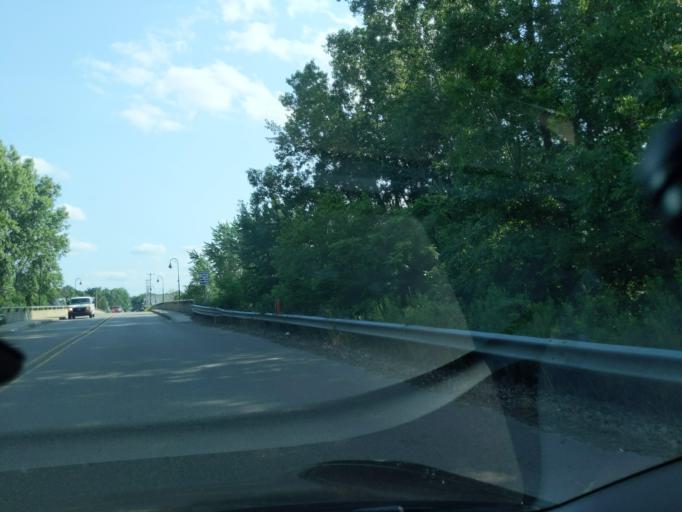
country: US
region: Michigan
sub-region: Ionia County
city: Saranac
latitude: 42.9341
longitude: -85.2134
